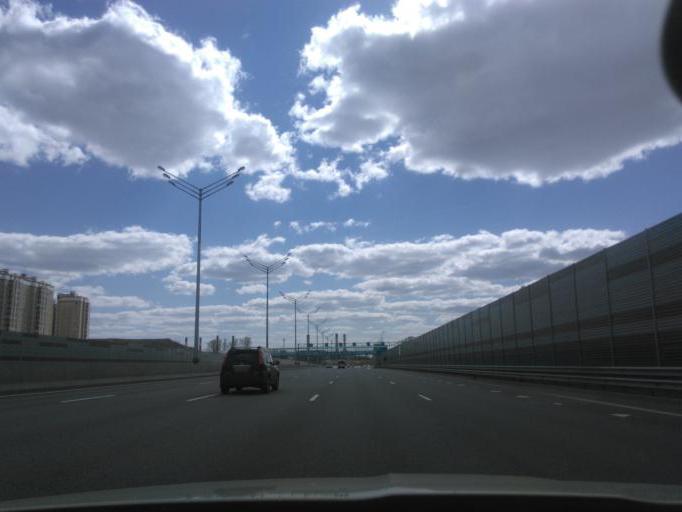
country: RU
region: Moskovskaya
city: Levoberezhnaya
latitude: 55.9082
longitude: 37.4738
